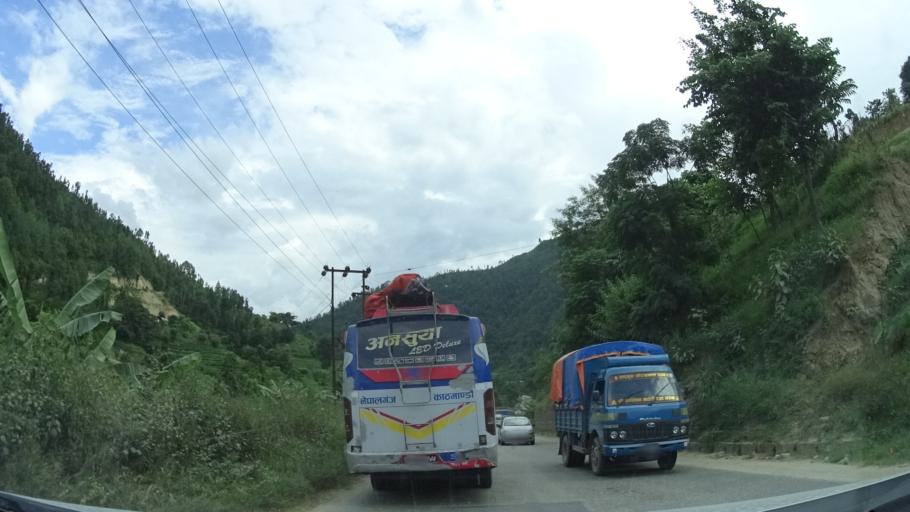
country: NP
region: Central Region
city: Kirtipur
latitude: 27.7793
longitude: 85.0237
